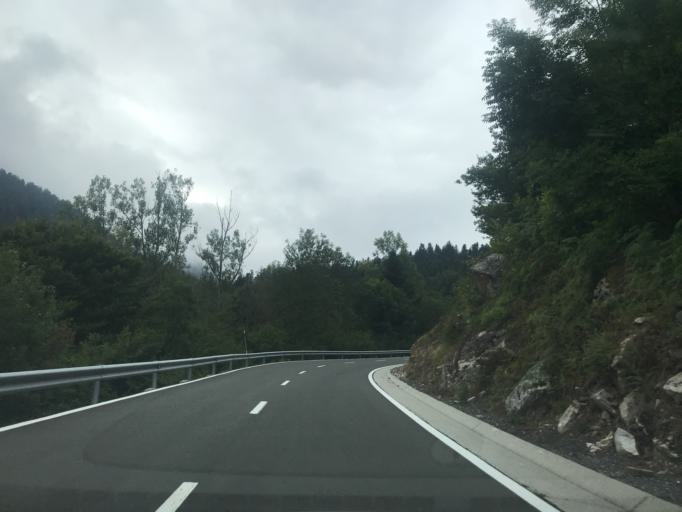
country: ES
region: Catalonia
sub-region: Provincia de Lleida
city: Les
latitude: 42.7681
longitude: 0.6708
